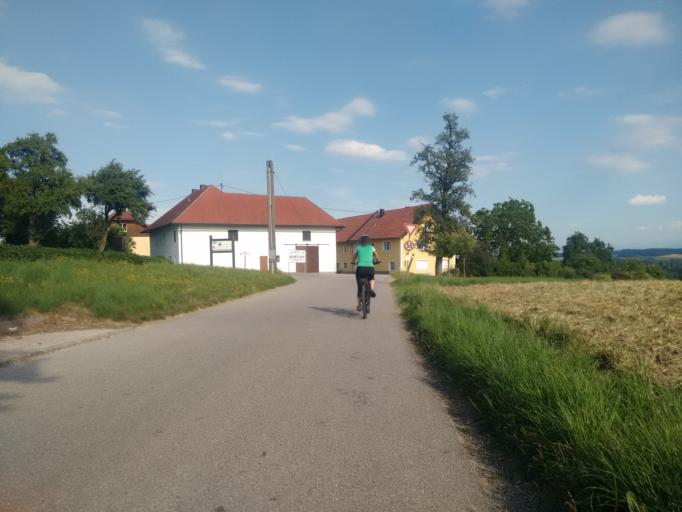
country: AT
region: Upper Austria
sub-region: Politischer Bezirk Grieskirchen
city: Bad Schallerbach
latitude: 48.2374
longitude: 13.9288
